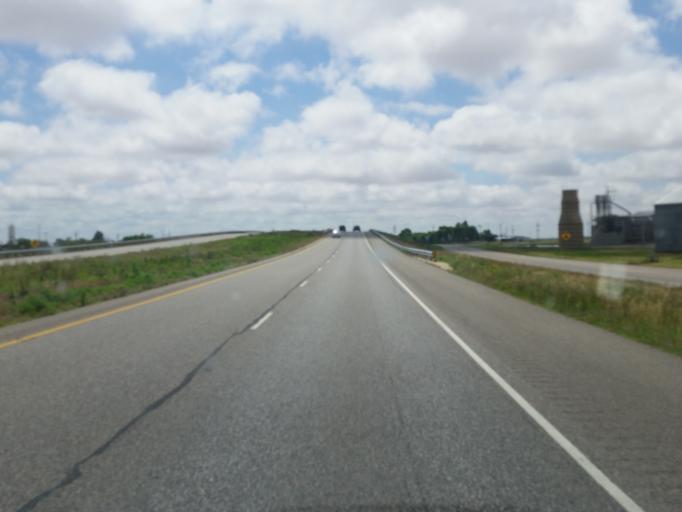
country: US
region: Texas
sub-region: Lubbock County
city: Slaton
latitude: 33.4214
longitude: -101.6454
